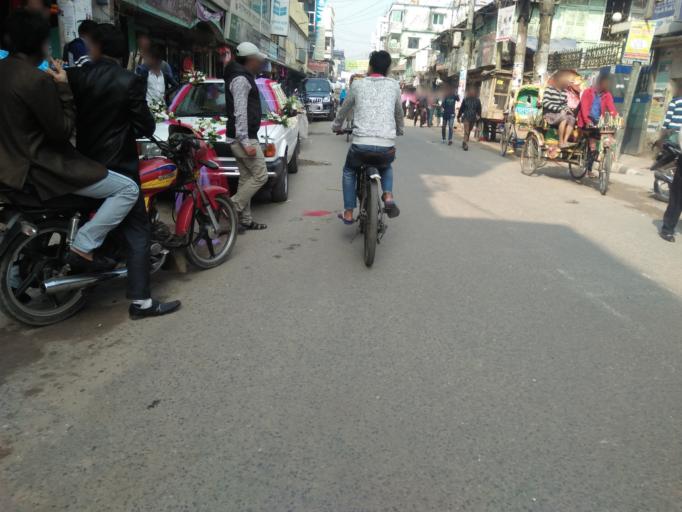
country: BD
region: Barisal
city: Bhola
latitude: 22.6838
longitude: 90.6455
